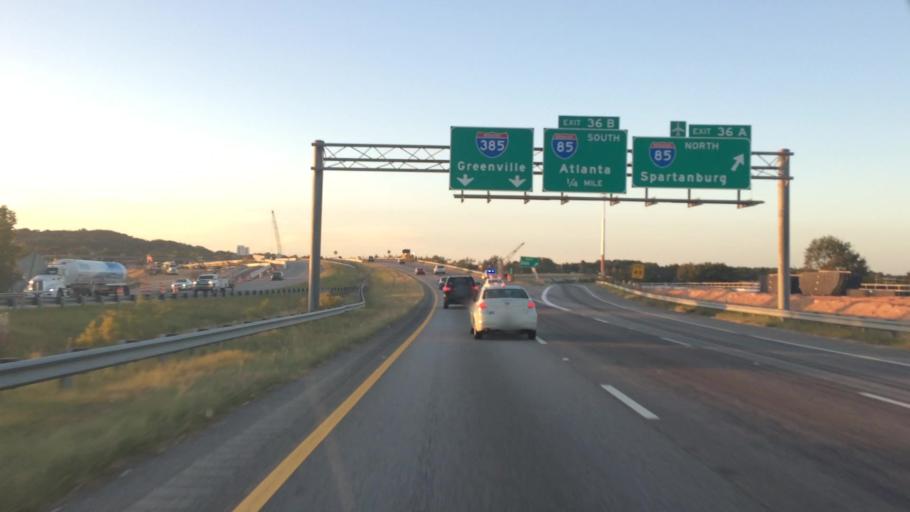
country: US
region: South Carolina
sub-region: Greenville County
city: Mauldin
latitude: 34.8294
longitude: -82.2939
